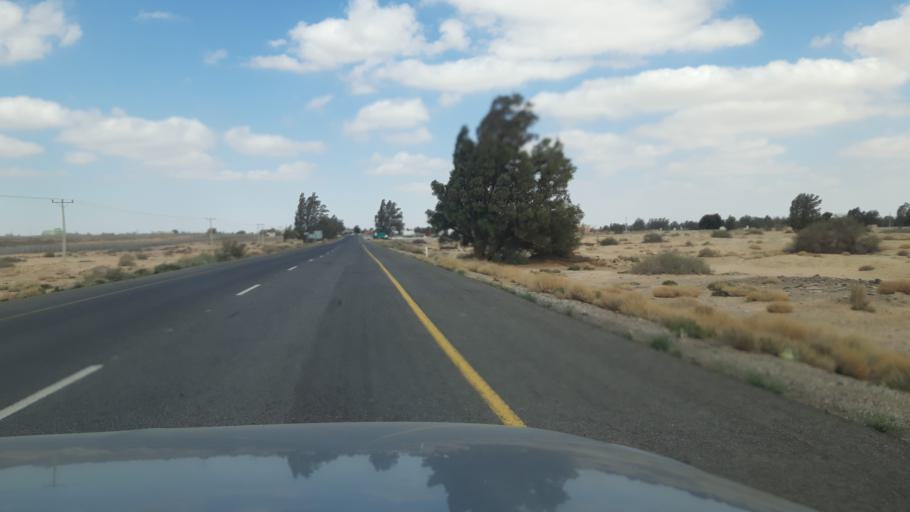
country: JO
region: Amman
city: Al Azraq ash Shamali
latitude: 31.8214
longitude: 36.8092
